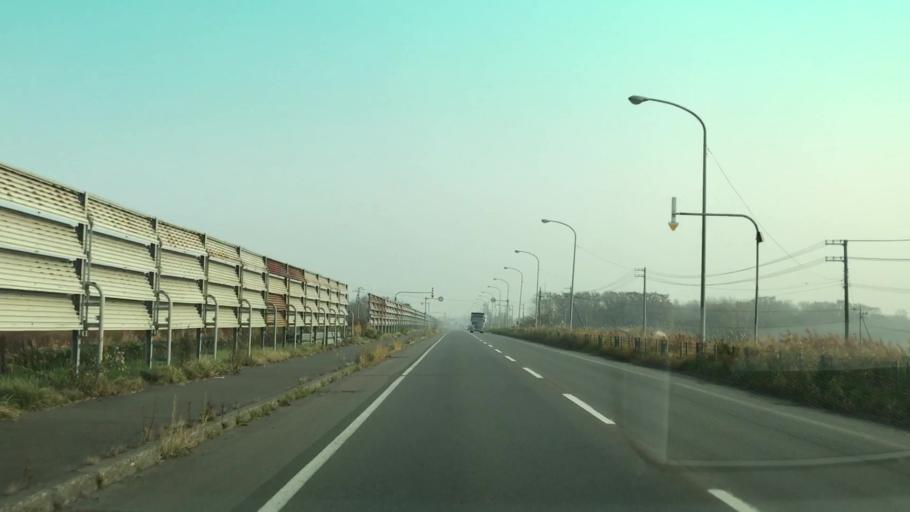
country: JP
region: Hokkaido
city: Ishikari
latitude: 43.2370
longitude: 141.3622
